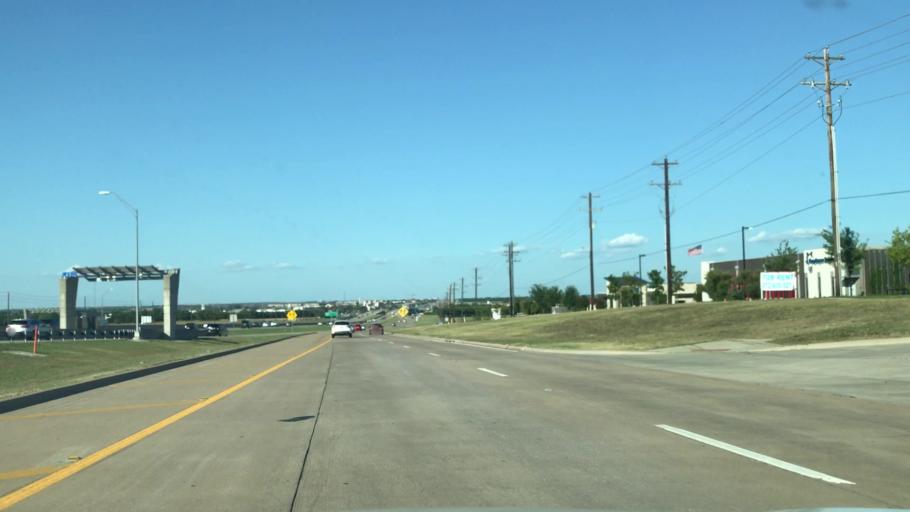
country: US
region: Texas
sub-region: Collin County
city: Frisco
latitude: 33.1130
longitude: -96.7648
